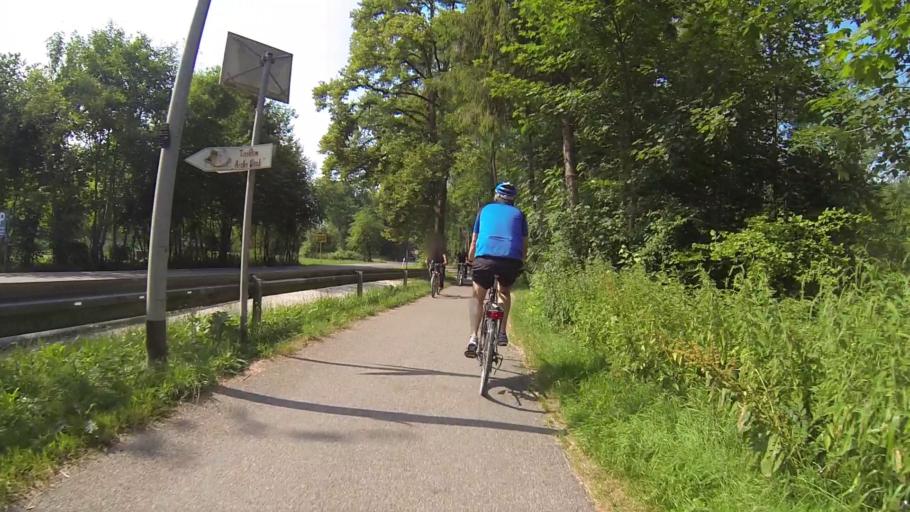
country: DE
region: Bavaria
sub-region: Swabia
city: Guenzburg
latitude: 48.4659
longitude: 10.2670
